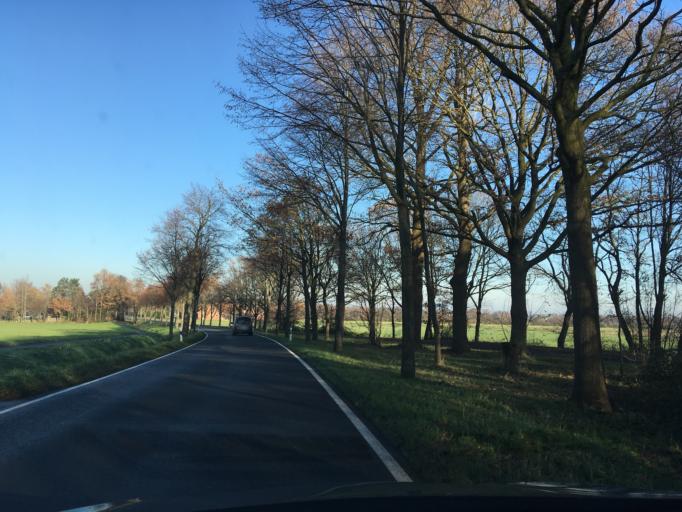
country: DE
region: North Rhine-Westphalia
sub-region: Regierungsbezirk Munster
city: Vreden
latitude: 52.1112
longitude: 6.8811
